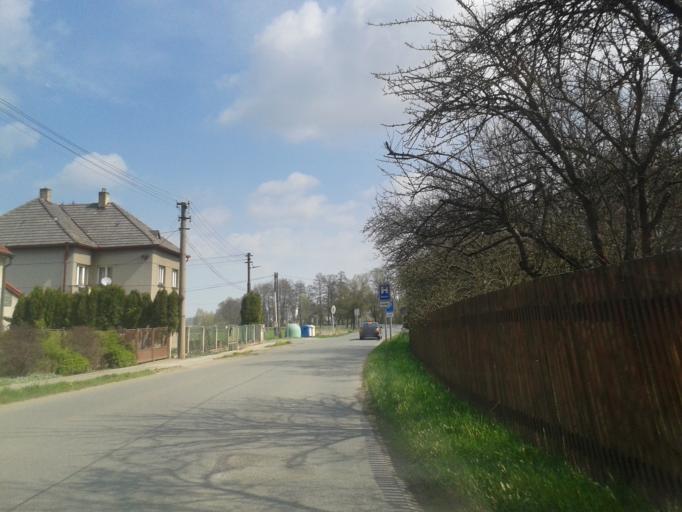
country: CZ
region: Central Bohemia
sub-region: Okres Beroun
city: Horovice
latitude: 49.8445
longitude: 13.9077
